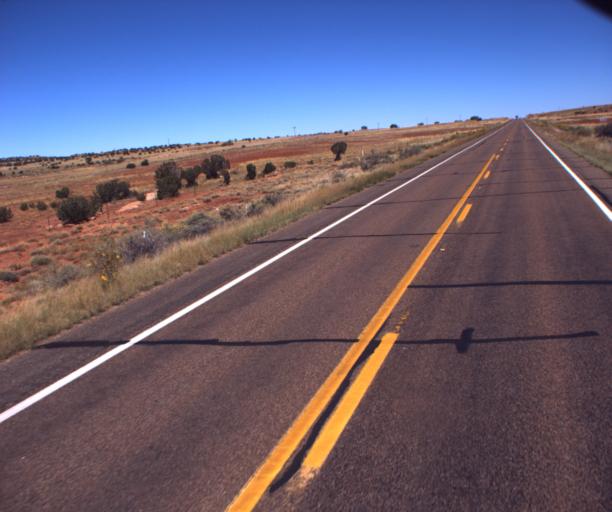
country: US
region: Arizona
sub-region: Apache County
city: Saint Johns
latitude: 34.4554
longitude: -109.4052
